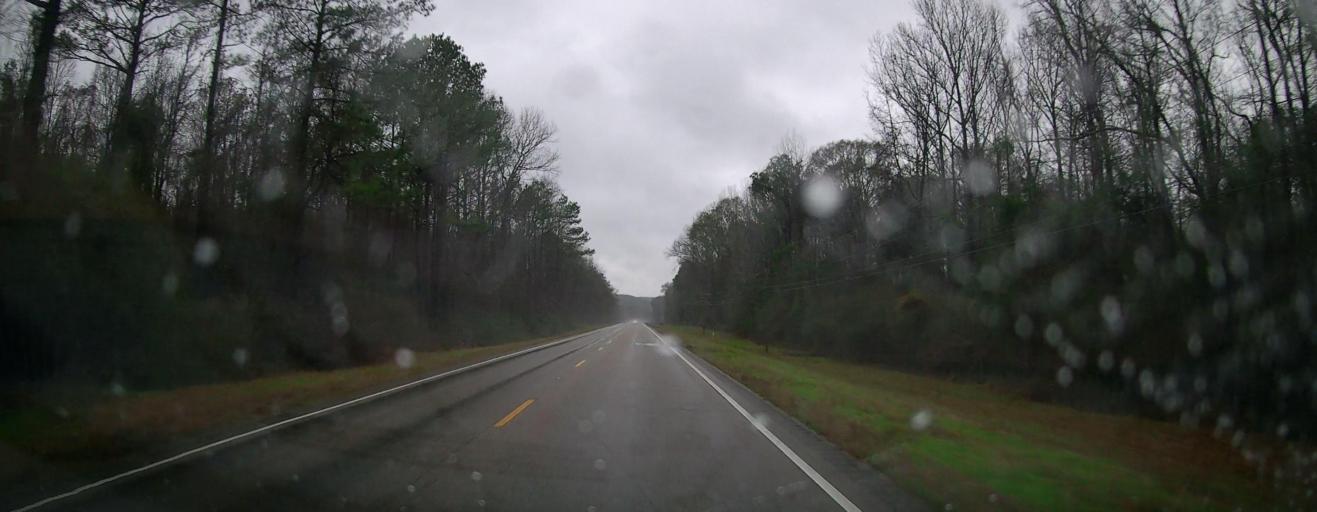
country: US
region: Alabama
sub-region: Autauga County
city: Prattville
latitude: 32.4904
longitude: -86.5532
